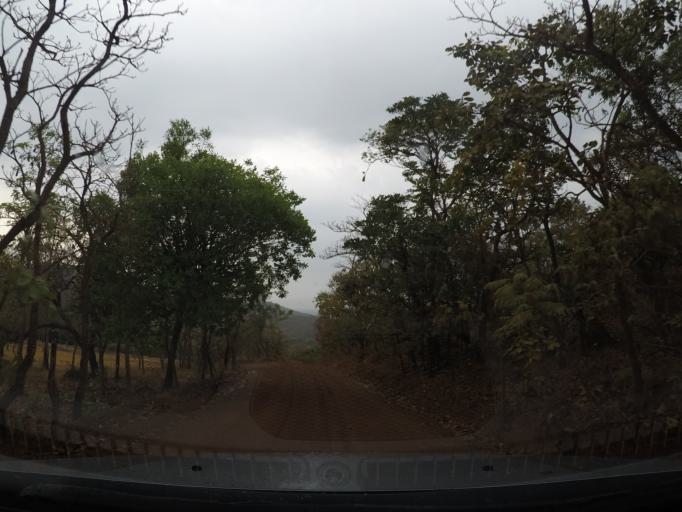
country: BR
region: Goias
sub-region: Pirenopolis
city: Pirenopolis
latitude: -15.8200
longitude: -48.8950
